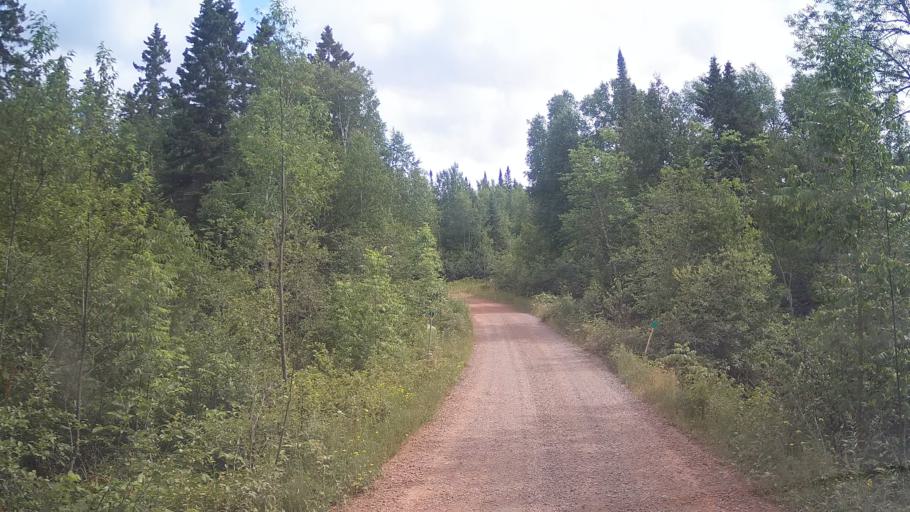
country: CA
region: Ontario
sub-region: Thunder Bay District
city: Thunder Bay
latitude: 48.6780
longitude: -88.6686
